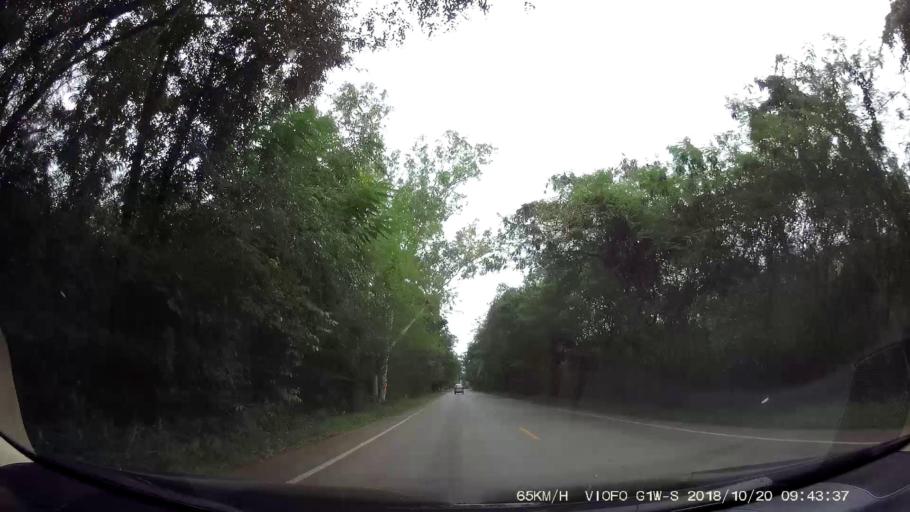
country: TH
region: Chaiyaphum
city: Khon San
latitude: 16.4753
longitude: 101.9473
